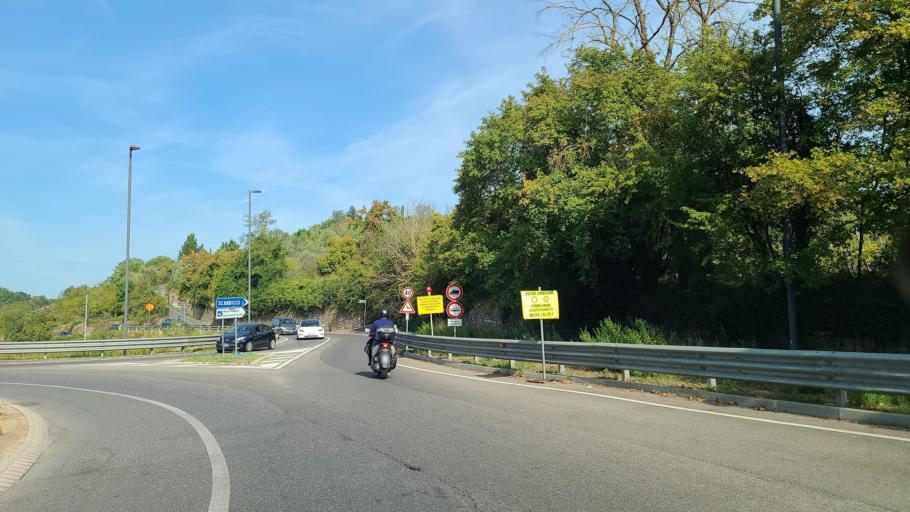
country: IT
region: Tuscany
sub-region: Province of Florence
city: Tavarnuzze
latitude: 43.7428
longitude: 11.2197
